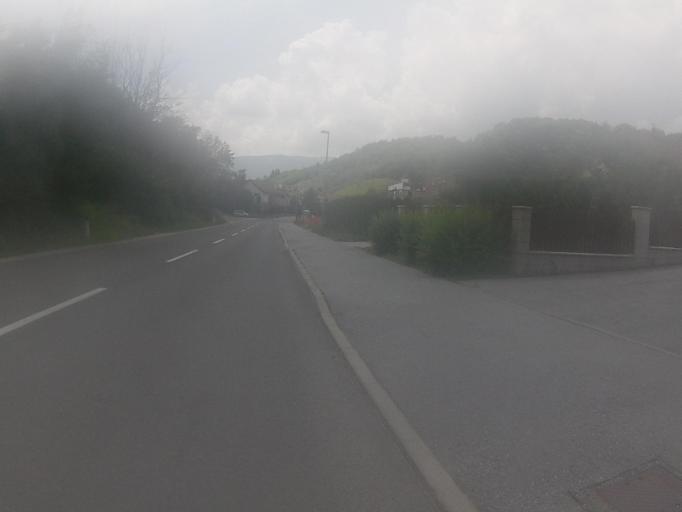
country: SI
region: Maribor
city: Kamnica
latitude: 46.5808
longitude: 15.6146
